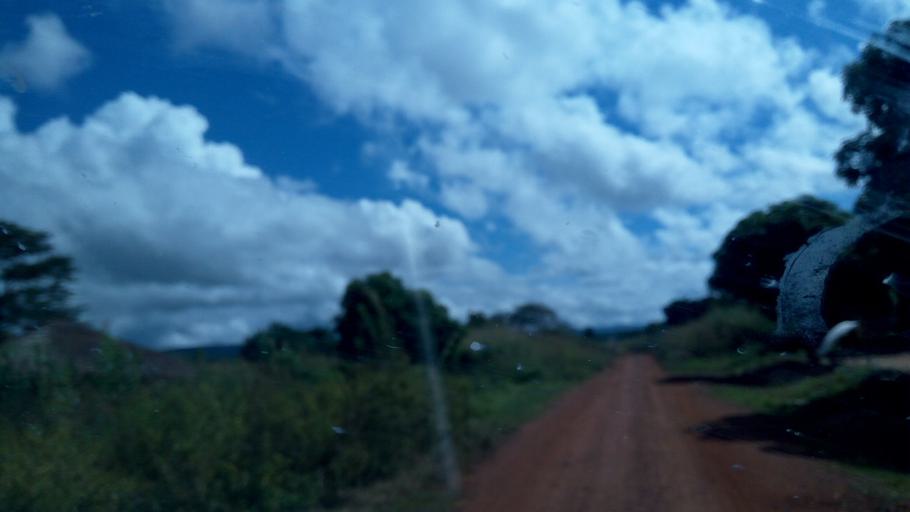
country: ZM
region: Northern
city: Kaputa
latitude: -8.3368
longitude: 28.9925
